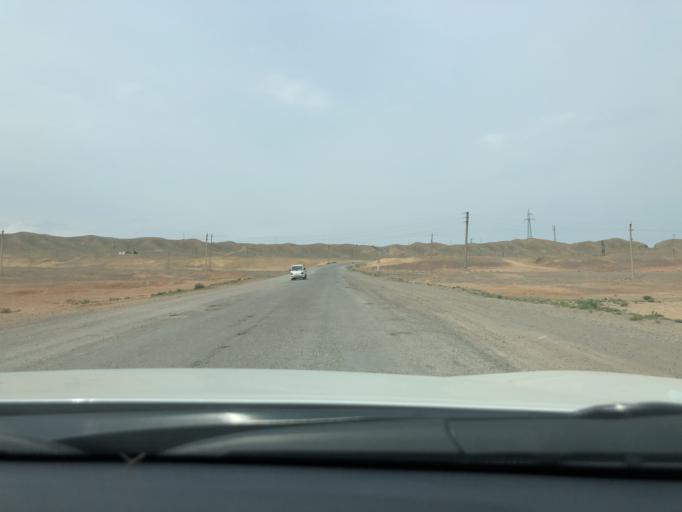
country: TJ
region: Viloyati Sughd
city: Kim
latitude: 40.2109
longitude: 70.4748
